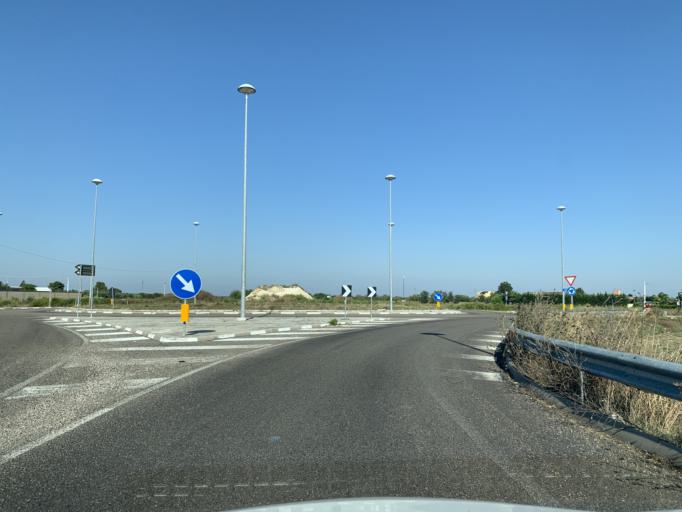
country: IT
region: Apulia
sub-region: Provincia di Lecce
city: Nardo
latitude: 40.1892
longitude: 18.0387
